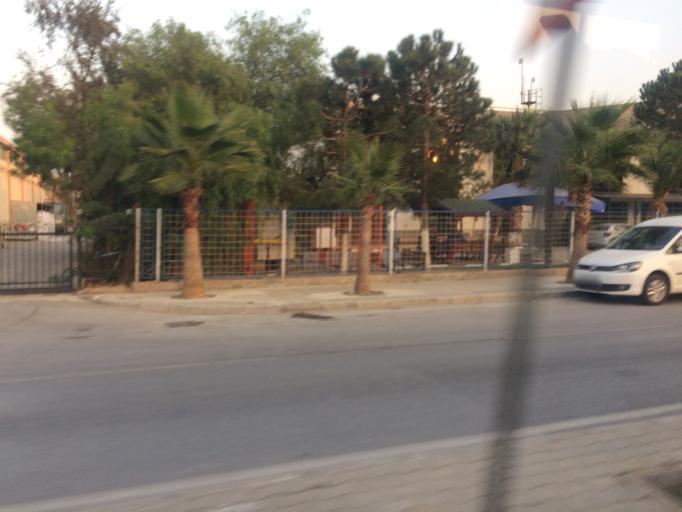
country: TR
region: Izmir
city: Karsiyaka
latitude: 38.4975
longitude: 27.0371
